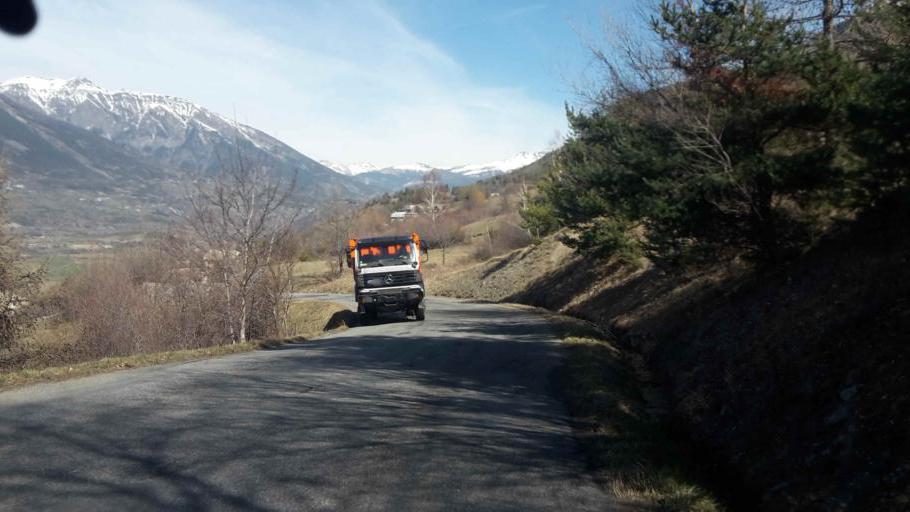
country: FR
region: Provence-Alpes-Cote d'Azur
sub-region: Departement des Hautes-Alpes
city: Embrun
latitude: 44.5776
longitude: 6.5316
